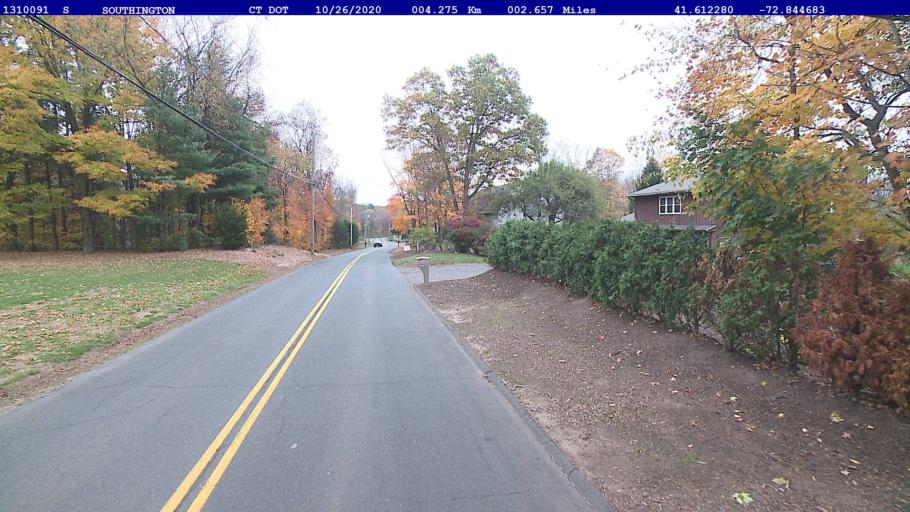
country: US
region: Connecticut
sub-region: Hartford County
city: Plainville
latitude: 41.6123
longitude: -72.8447
